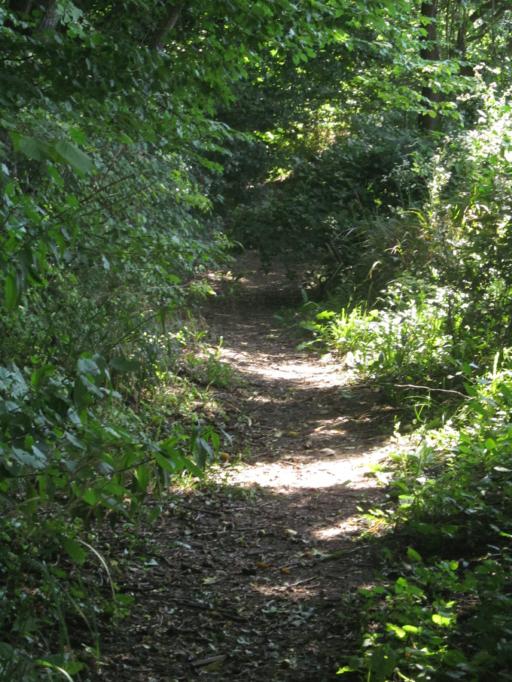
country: HU
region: Pest
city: Pilisszentkereszt
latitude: 47.6874
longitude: 18.9007
